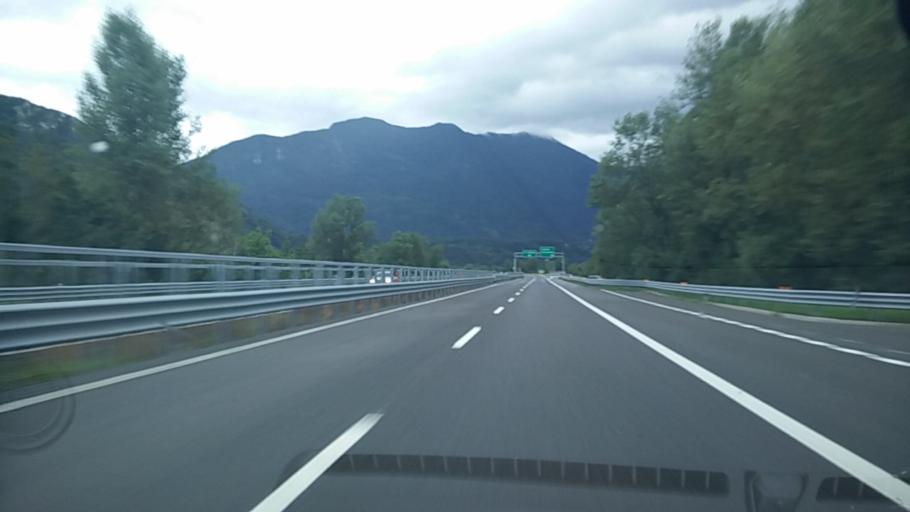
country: IT
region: Friuli Venezia Giulia
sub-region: Provincia di Udine
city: Amaro
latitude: 46.3686
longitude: 13.0857
